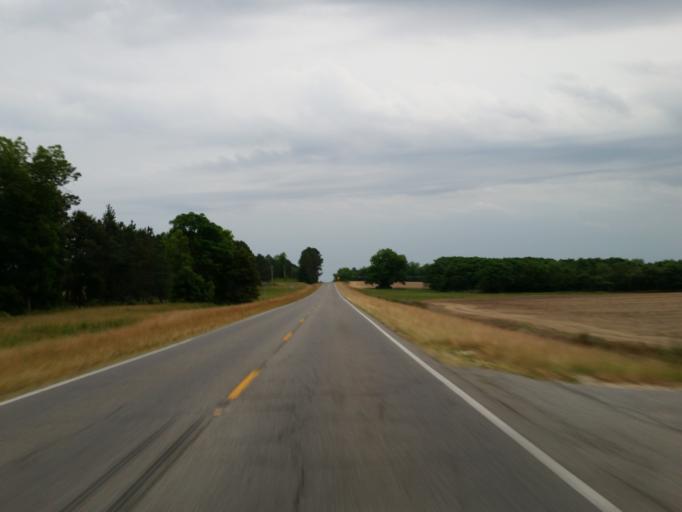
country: US
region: Georgia
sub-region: Crisp County
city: Cordele
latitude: 32.0162
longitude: -83.7917
